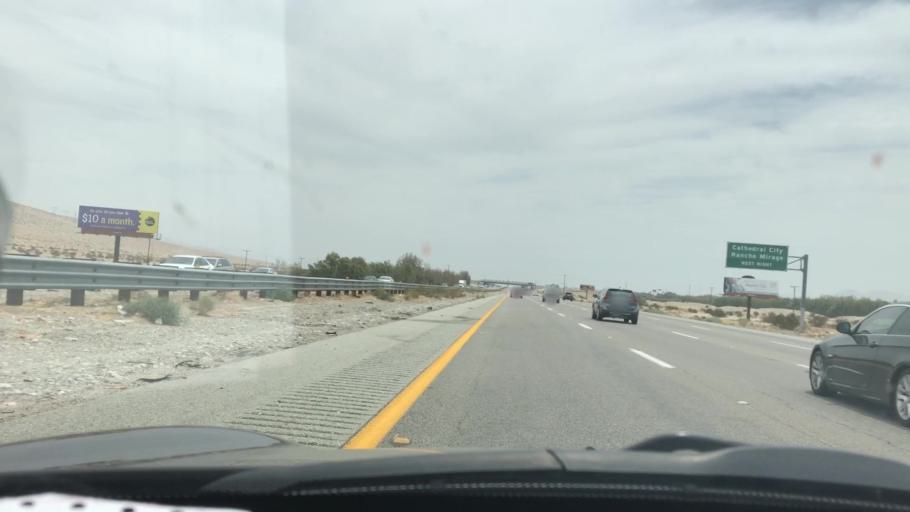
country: US
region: California
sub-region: Riverside County
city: Desert Edge
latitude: 33.8561
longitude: -116.4699
